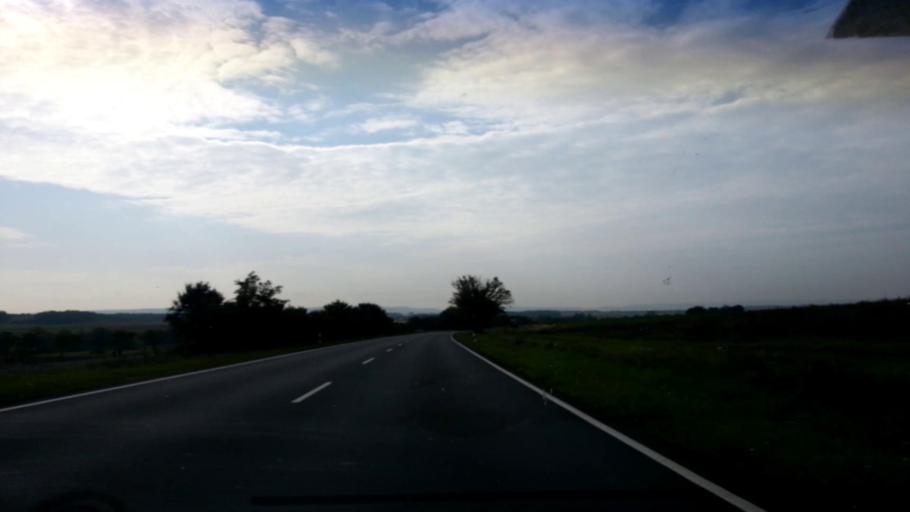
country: DE
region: Bavaria
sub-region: Regierungsbezirk Unterfranken
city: Lulsfeld
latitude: 49.8547
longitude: 10.3518
